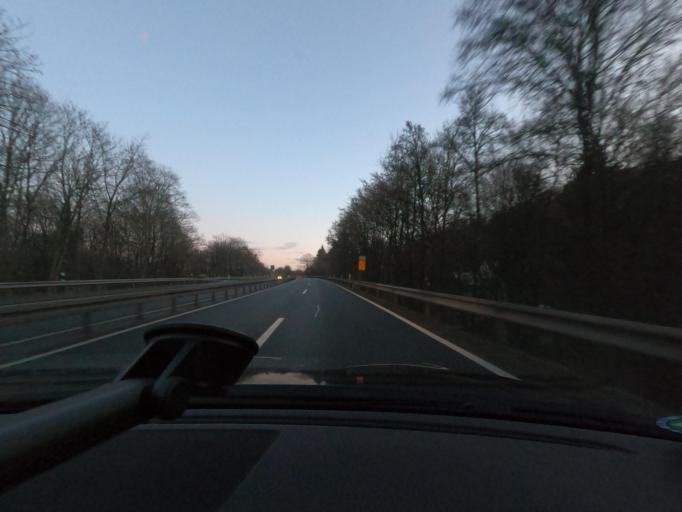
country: DE
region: Lower Saxony
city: Osterode am Harz
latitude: 51.7257
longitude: 10.2426
